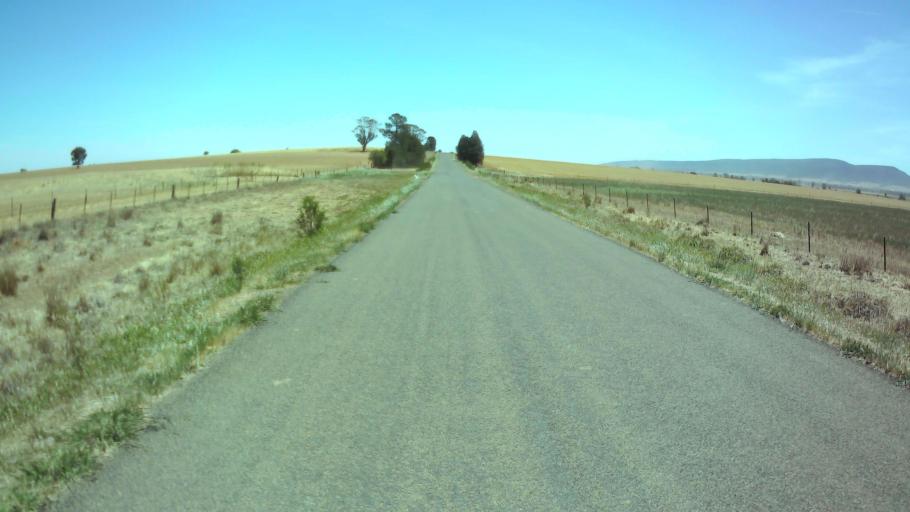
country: AU
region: New South Wales
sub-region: Weddin
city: Grenfell
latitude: -34.0505
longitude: 148.1873
